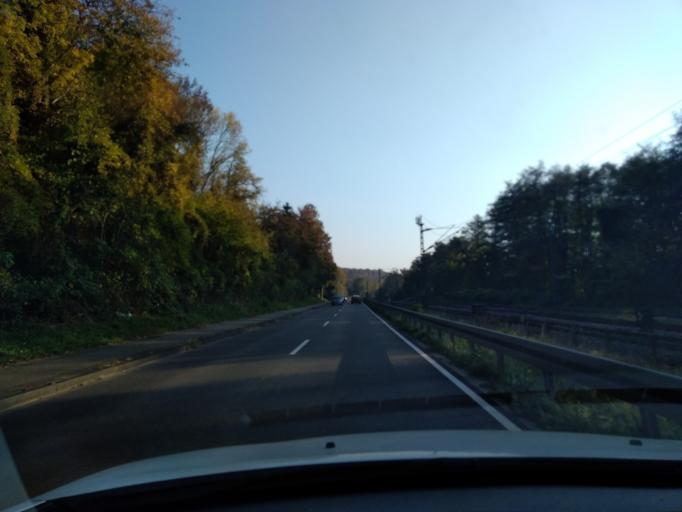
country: DE
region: Saarland
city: Kleinblittersdorf
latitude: 49.1407
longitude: 7.0460
